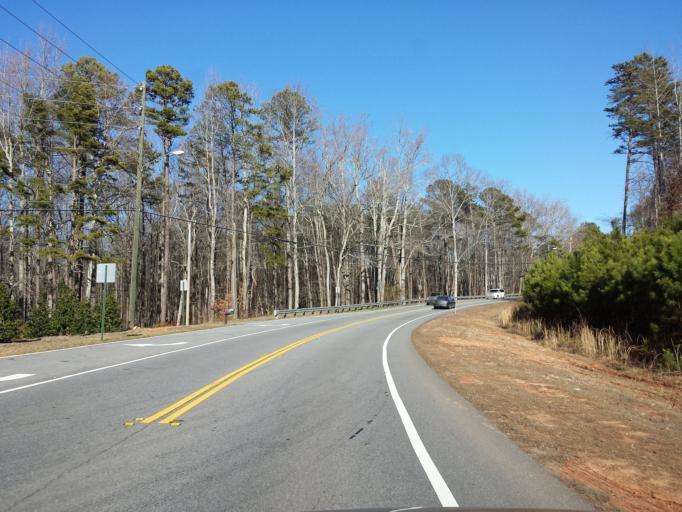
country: US
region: Georgia
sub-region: Cobb County
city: Kennesaw
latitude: 33.9650
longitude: -84.6584
